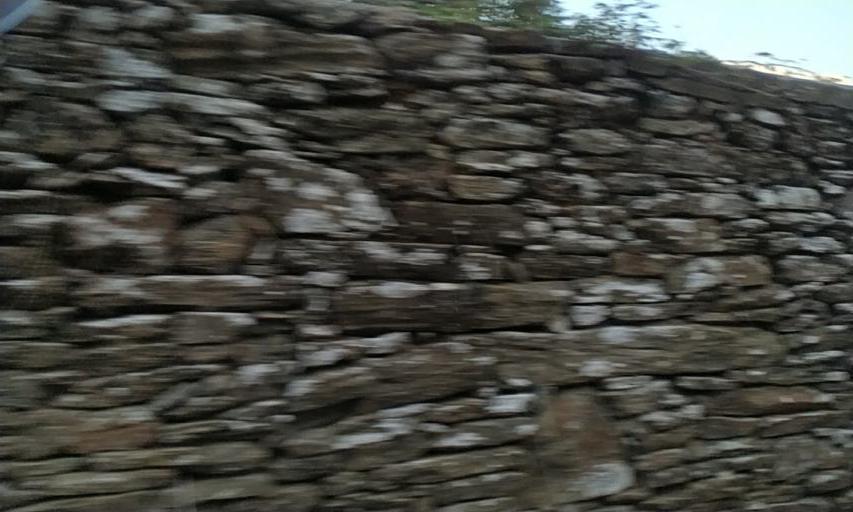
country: PT
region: Vila Real
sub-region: Mesao Frio
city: Mesao Frio
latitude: 41.1766
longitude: -7.8448
